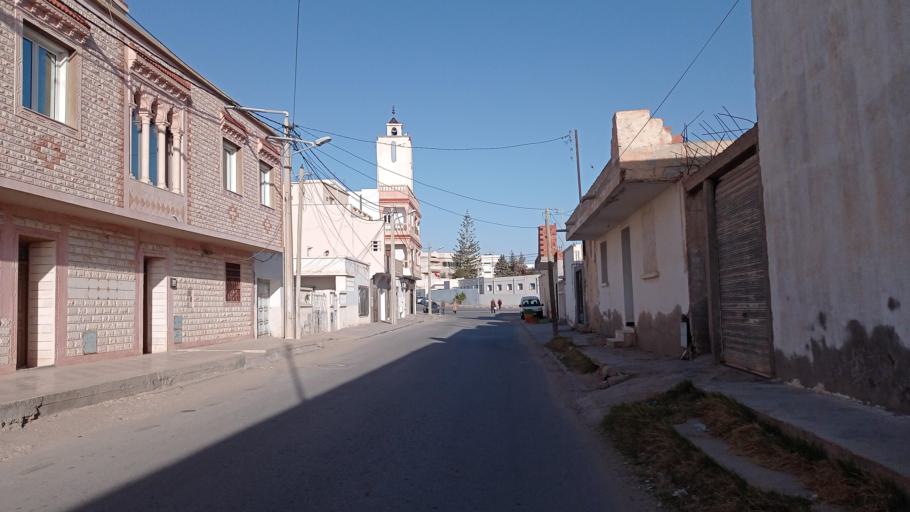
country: TN
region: Qabis
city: Gabes
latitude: 33.8592
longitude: 10.1171
